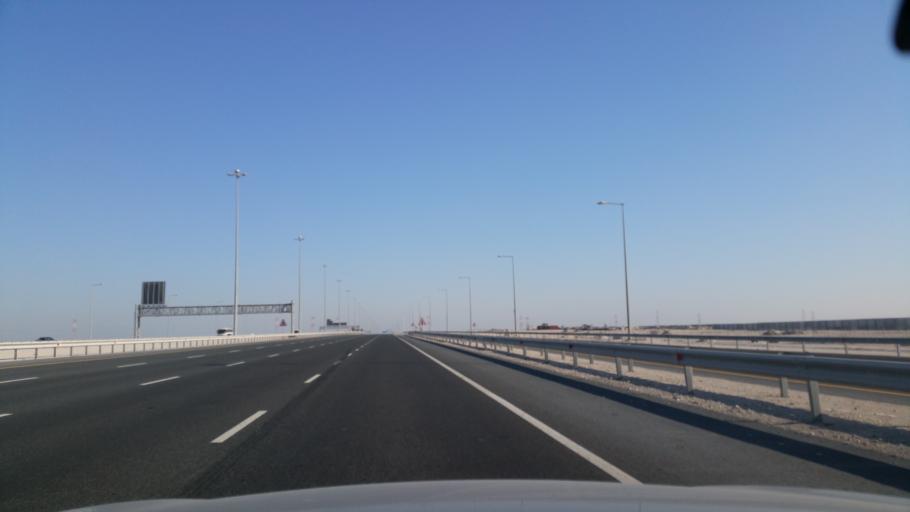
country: QA
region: Al Wakrah
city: Al Wukayr
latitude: 25.1174
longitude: 51.4920
